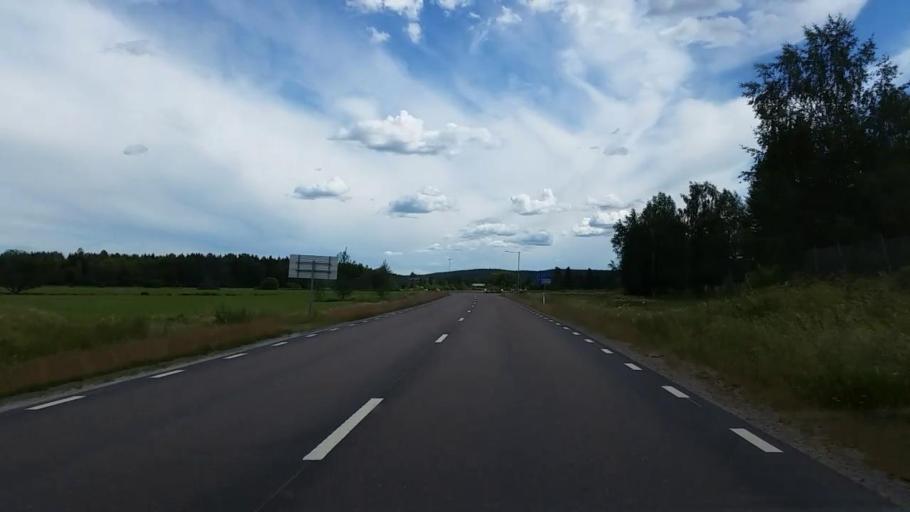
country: SE
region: Gaevleborg
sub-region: Ovanakers Kommun
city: Edsbyn
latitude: 61.3745
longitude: 15.8430
